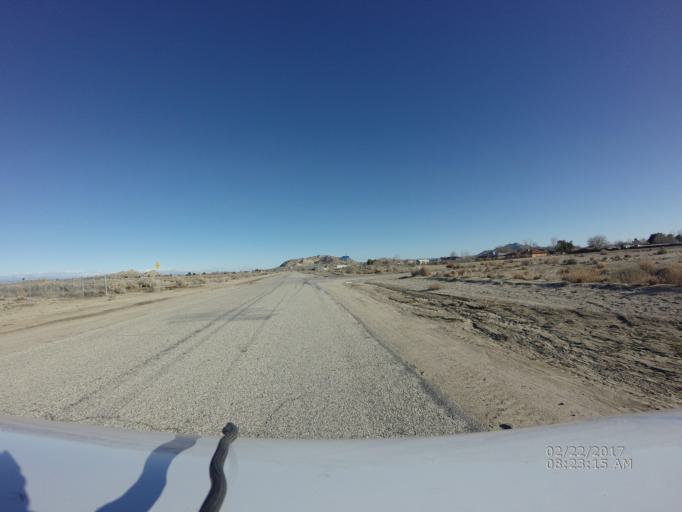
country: US
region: California
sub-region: Los Angeles County
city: Lake Los Angeles
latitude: 34.6236
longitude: -117.8536
